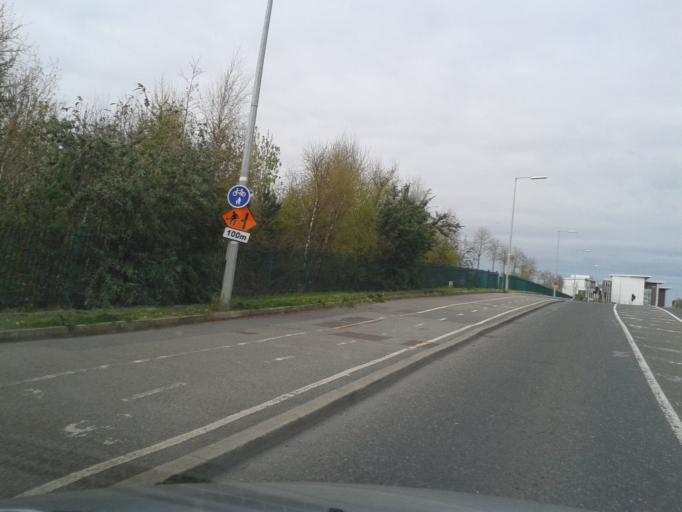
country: IE
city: Fairview
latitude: 53.3585
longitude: -6.2335
